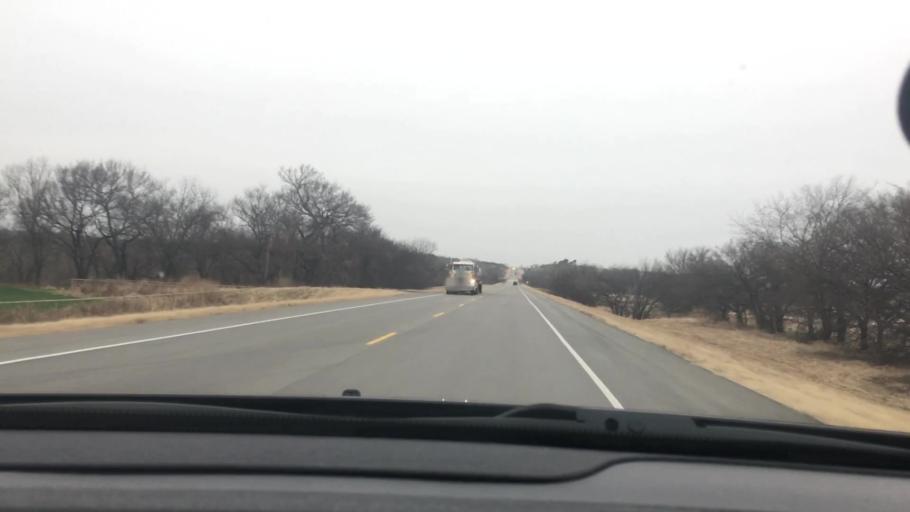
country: US
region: Oklahoma
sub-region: Garvin County
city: Wynnewood
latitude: 34.6227
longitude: -97.1908
